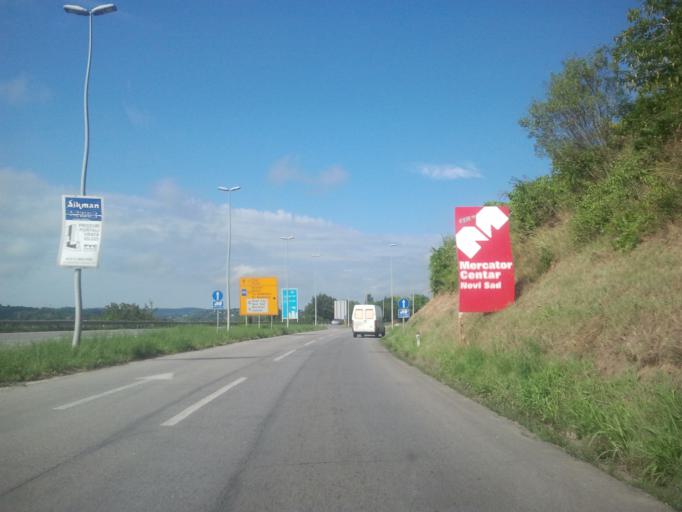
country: RS
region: Autonomna Pokrajina Vojvodina
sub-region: Juznobacki Okrug
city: Petrovaradin
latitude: 45.2250
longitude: 19.8773
